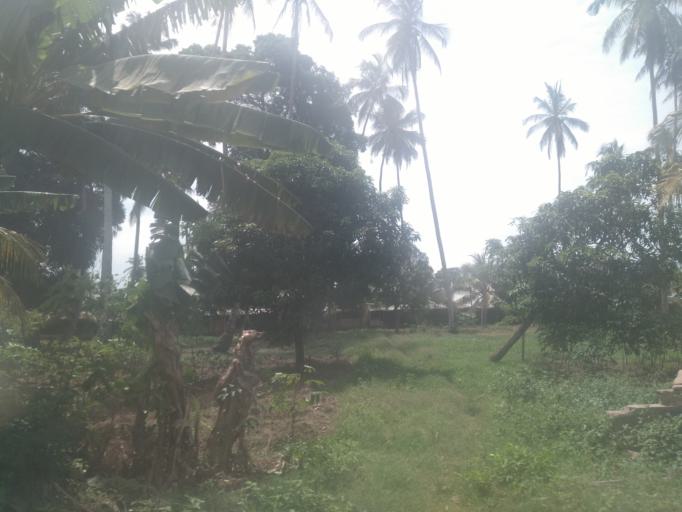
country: TZ
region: Zanzibar Urban/West
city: Zanzibar
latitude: -6.2296
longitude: 39.2167
